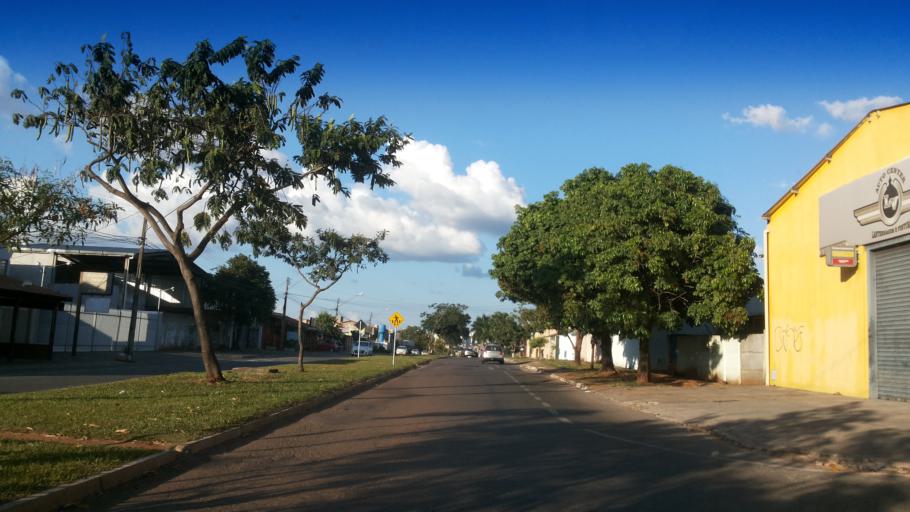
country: BR
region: Goias
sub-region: Goiania
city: Goiania
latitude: -16.7272
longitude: -49.3056
